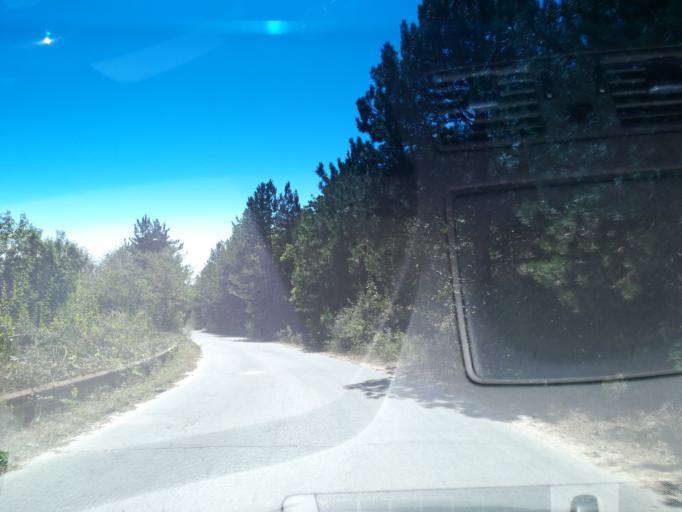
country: BG
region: Pazardzhik
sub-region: Obshtina Strelcha
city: Strelcha
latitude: 42.5323
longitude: 24.3310
